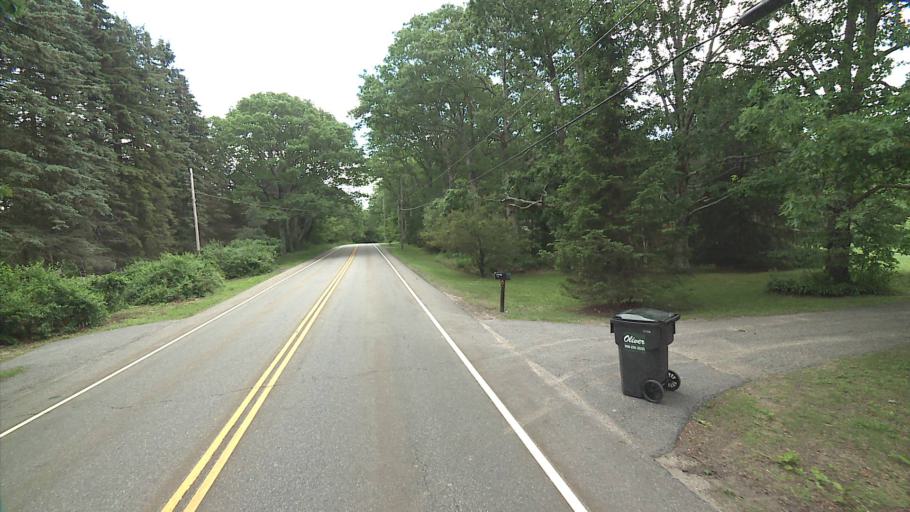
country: US
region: Connecticut
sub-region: Litchfield County
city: Winchester Center
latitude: 41.8799
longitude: -73.2517
